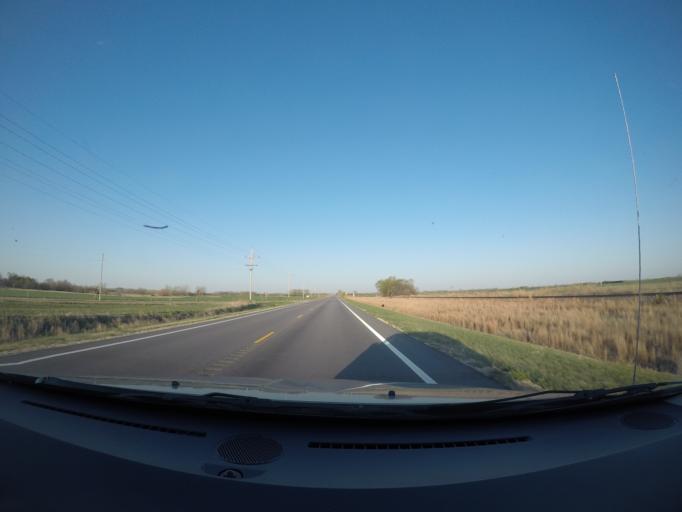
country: US
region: Kansas
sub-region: Stafford County
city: Stafford
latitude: 37.8396
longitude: -98.3585
